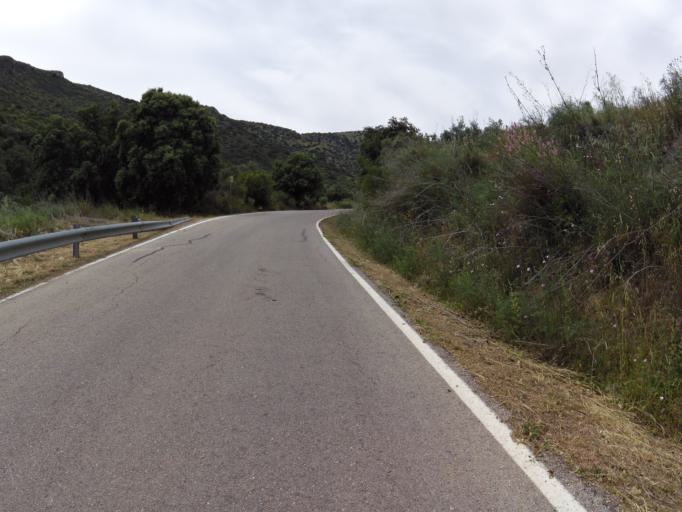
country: ES
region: Andalusia
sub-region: Province of Cordoba
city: Fuente-Tojar
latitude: 37.5184
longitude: -4.2123
